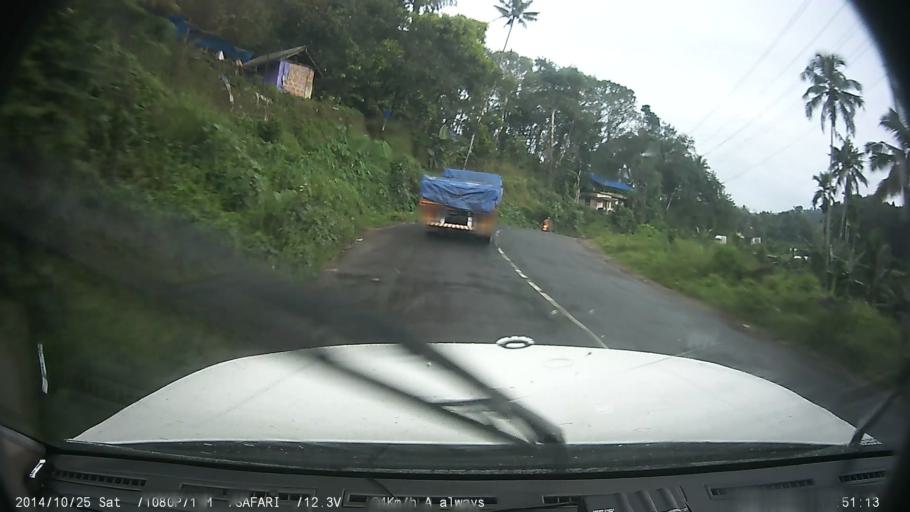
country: IN
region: Kerala
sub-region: Ernakulam
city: Muvattupuzha
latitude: 9.8958
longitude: 76.5871
